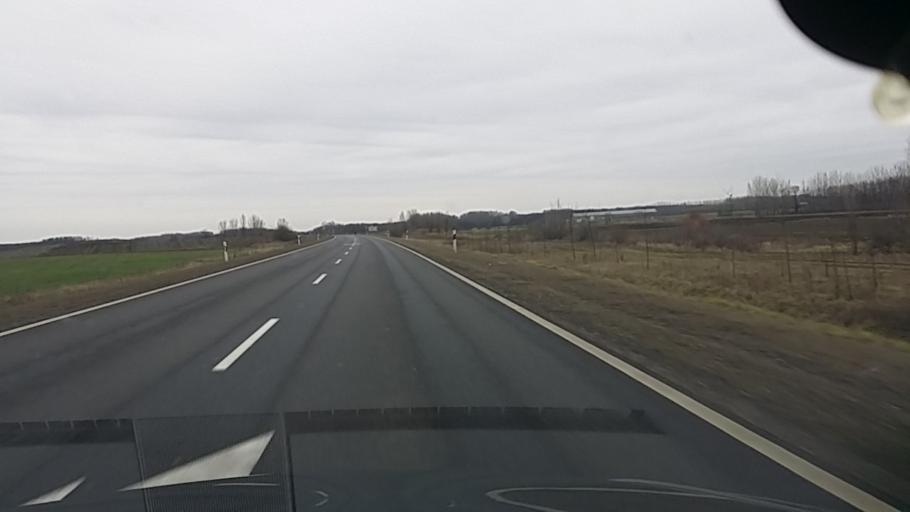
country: HU
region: Szabolcs-Szatmar-Bereg
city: Nyirpazony
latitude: 47.9394
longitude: 21.8184
